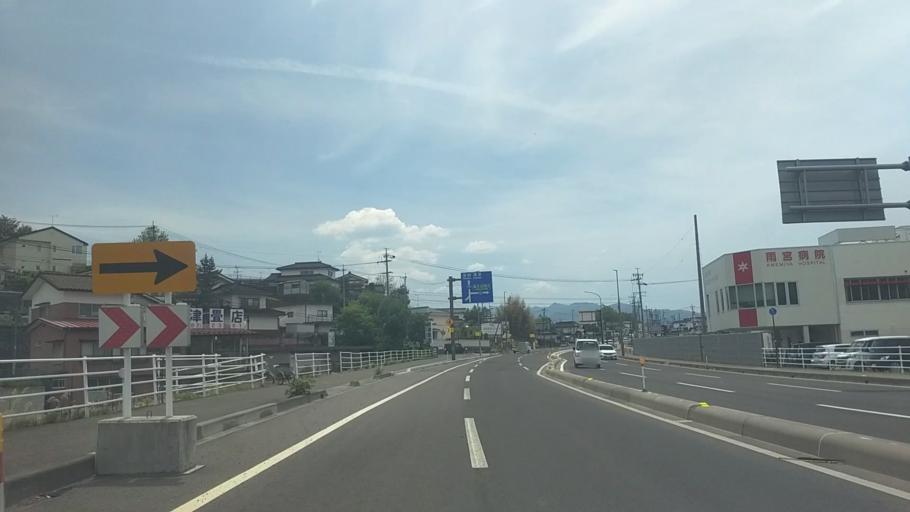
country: JP
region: Nagano
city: Saku
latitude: 36.1931
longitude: 138.4791
